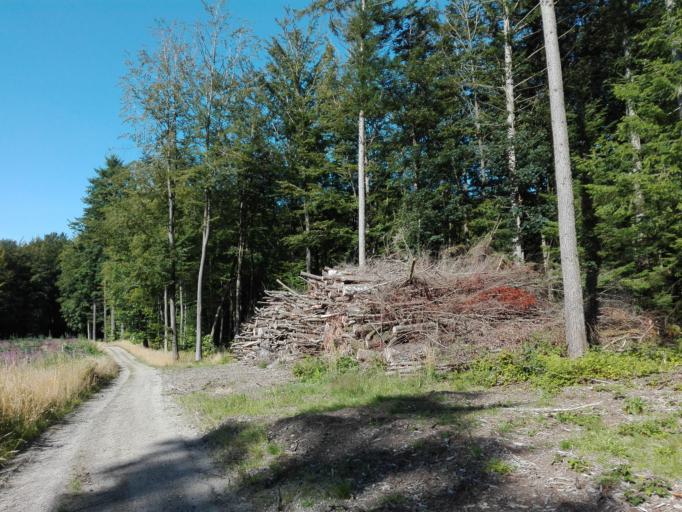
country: DK
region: Central Jutland
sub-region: Odder Kommune
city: Odder
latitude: 55.9686
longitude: 10.1251
